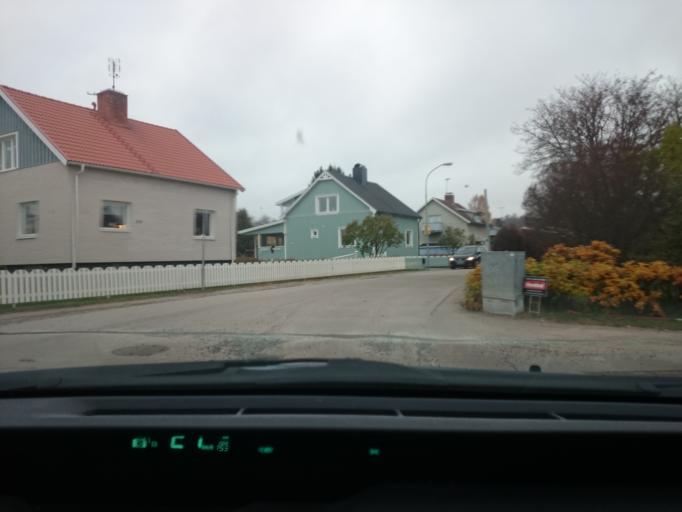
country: SE
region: Dalarna
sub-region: Saters Kommun
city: Saeter
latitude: 60.3503
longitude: 15.7462
